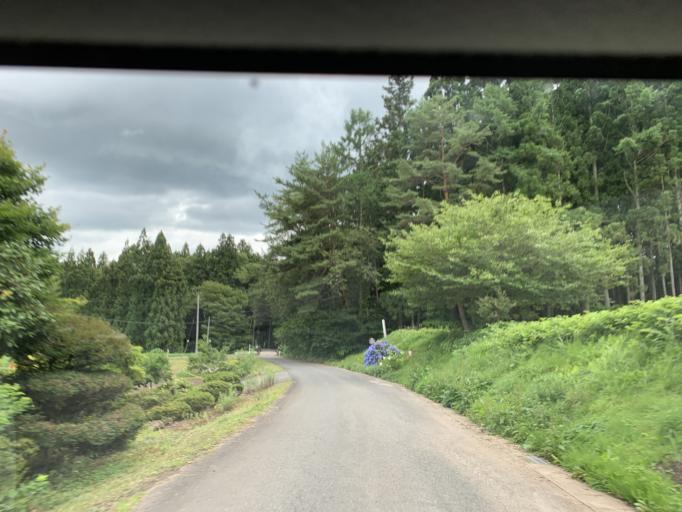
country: JP
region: Iwate
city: Ichinoseki
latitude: 38.9547
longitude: 141.0130
